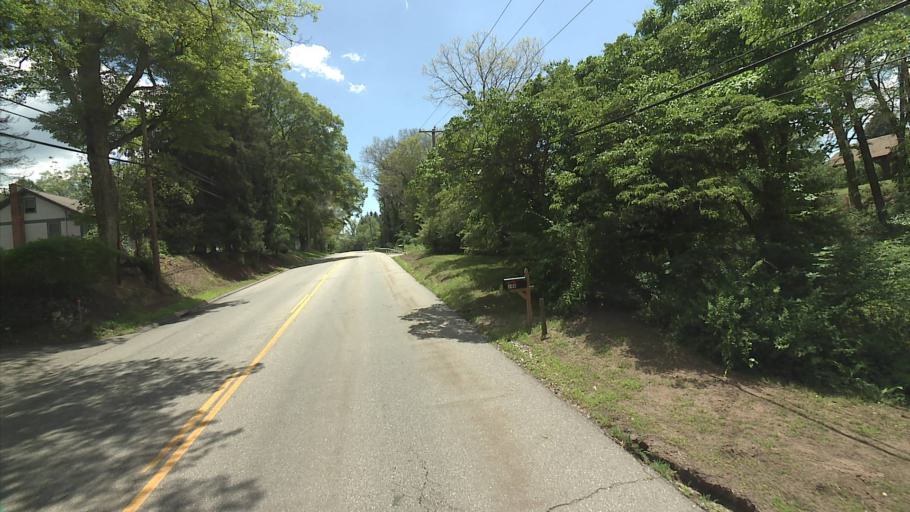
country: US
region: Connecticut
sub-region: Middlesex County
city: Moodus
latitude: 41.5085
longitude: -72.4791
